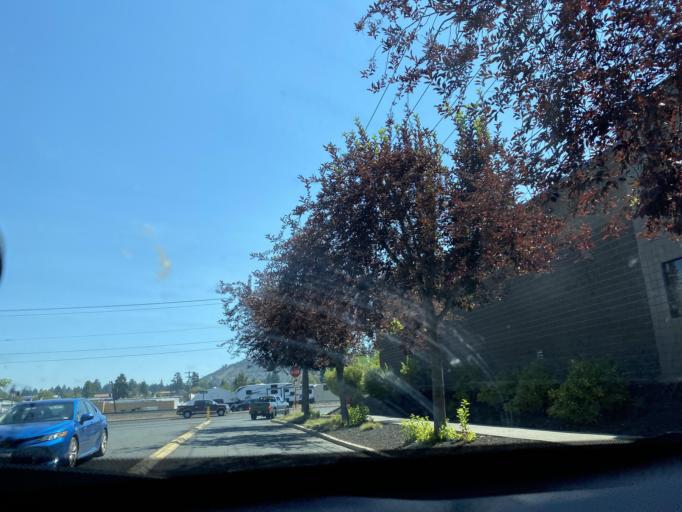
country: US
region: Oregon
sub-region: Deschutes County
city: Bend
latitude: 44.0619
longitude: -121.3081
